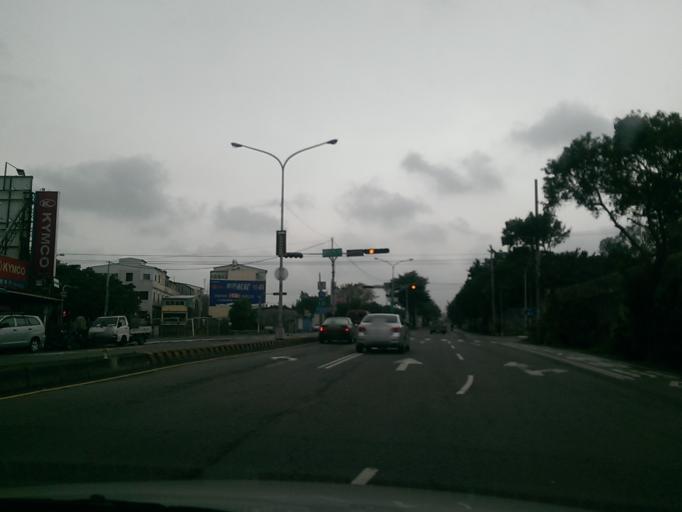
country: TW
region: Taiwan
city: Fengyuan
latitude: 24.2438
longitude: 120.6159
